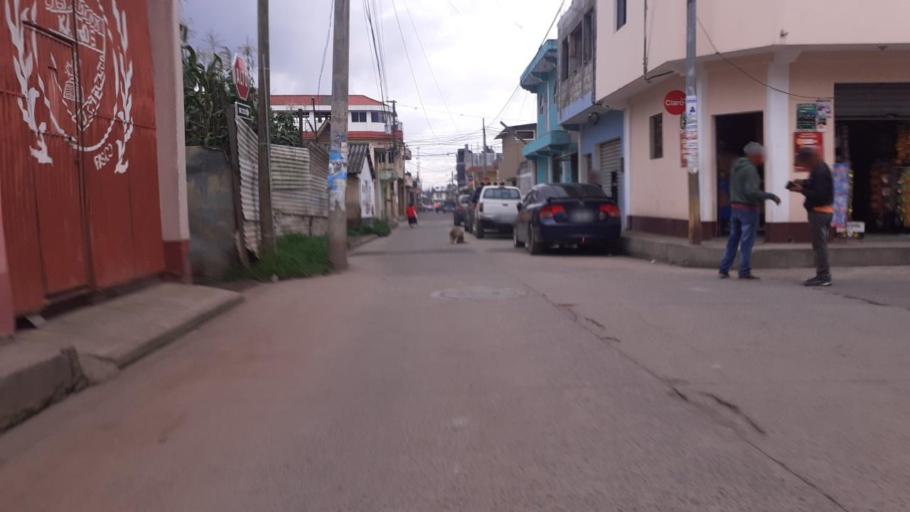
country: GT
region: Quetzaltenango
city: Ostuncalco
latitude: 14.8707
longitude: -91.6204
